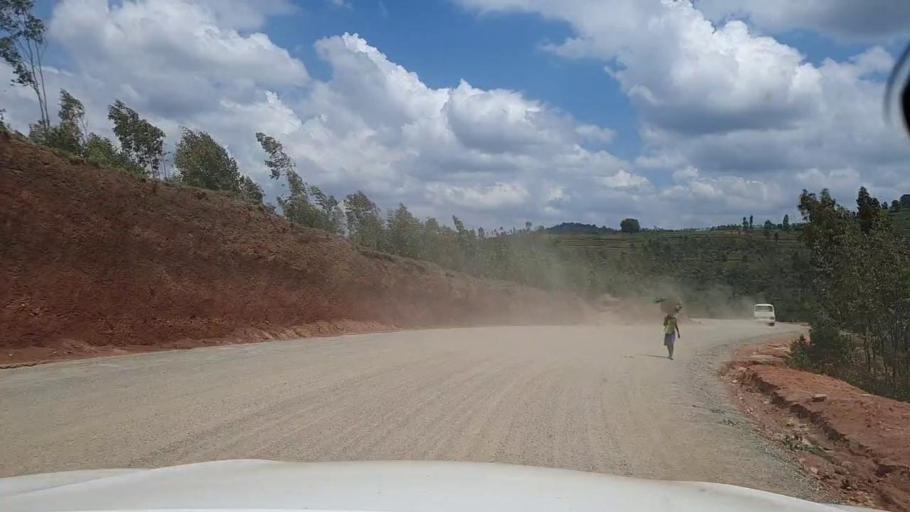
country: RW
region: Southern Province
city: Butare
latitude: -2.6950
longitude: 29.5589
